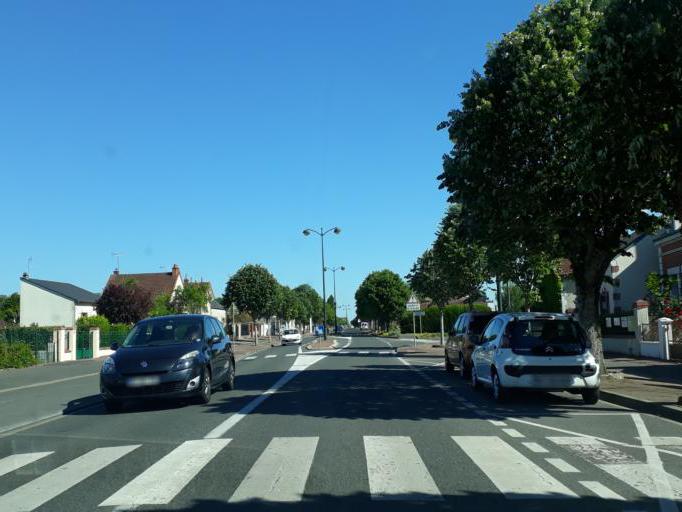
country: FR
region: Centre
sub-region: Departement du Loiret
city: Briare
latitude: 47.6346
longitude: 2.7435
